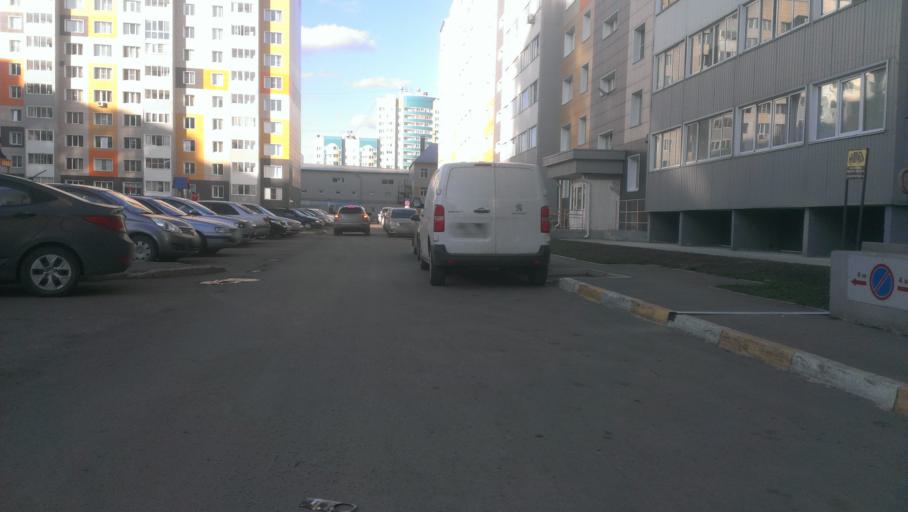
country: RU
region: Altai Krai
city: Novosilikatnyy
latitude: 53.3382
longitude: 83.6601
